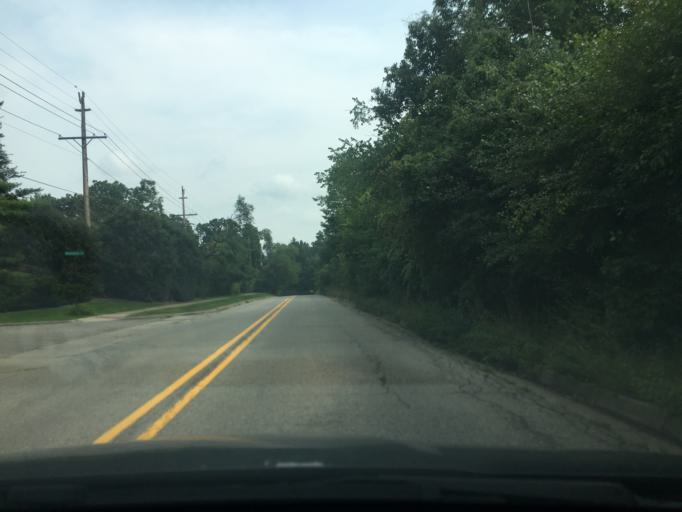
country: US
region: Michigan
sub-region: Oakland County
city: Birmingham
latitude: 42.5625
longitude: -83.2113
